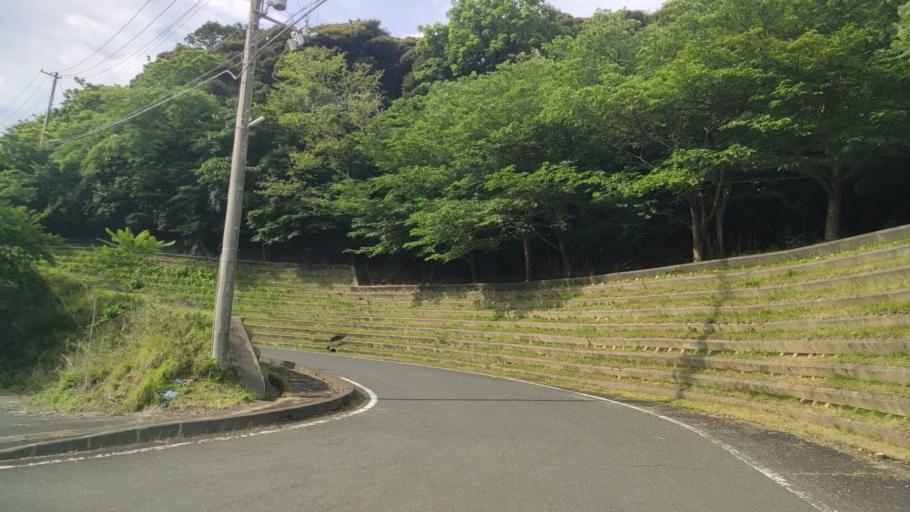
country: JP
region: Hyogo
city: Toyooka
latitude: 35.6426
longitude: 134.8983
